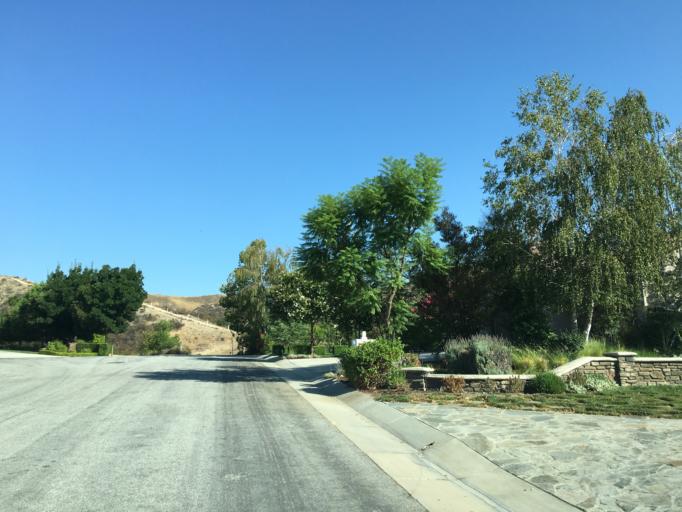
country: US
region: California
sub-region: Los Angeles County
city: Val Verde
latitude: 34.4664
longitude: -118.6698
